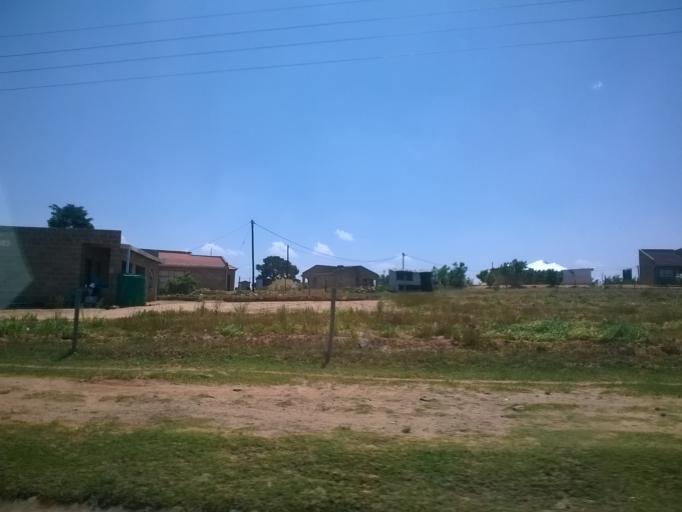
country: LS
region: Leribe
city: Maputsoe
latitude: -28.9743
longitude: 27.9795
